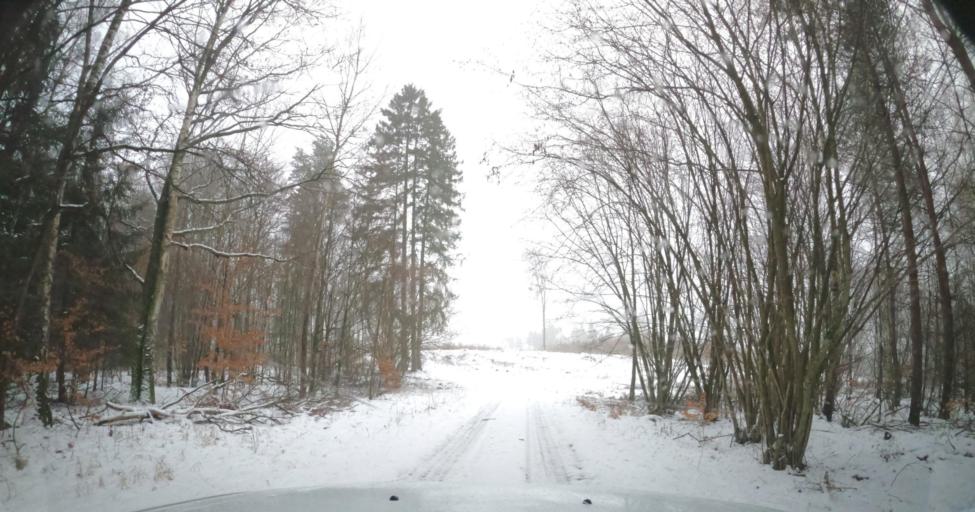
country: PL
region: West Pomeranian Voivodeship
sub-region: Powiat goleniowski
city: Przybiernow
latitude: 53.7110
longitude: 14.8781
